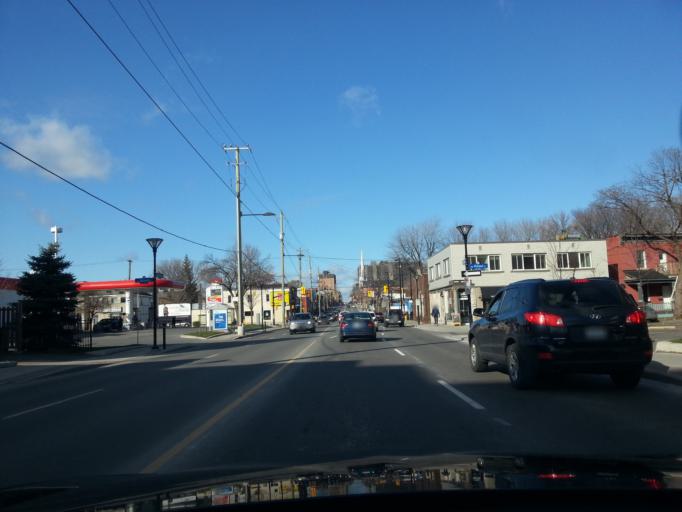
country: CA
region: Ontario
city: Ottawa
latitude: 45.4070
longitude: -75.7031
